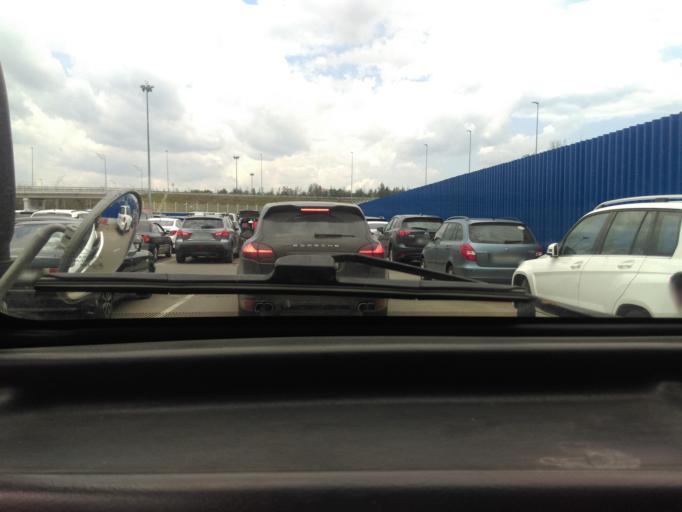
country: RU
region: Moskovskaya
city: Yakovlevskoye
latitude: 55.4182
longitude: 37.9032
